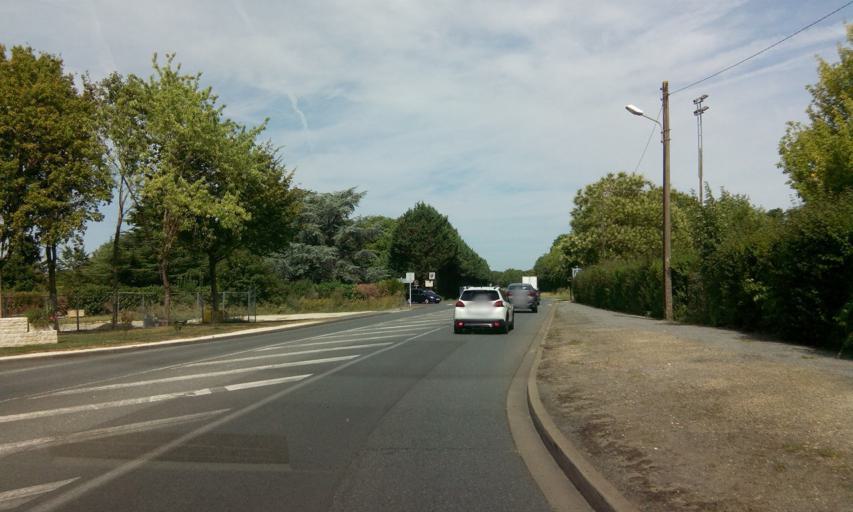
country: FR
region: Poitou-Charentes
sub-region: Departement des Deux-Sevres
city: Sauze-Vaussais
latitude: 46.1339
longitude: 0.1123
